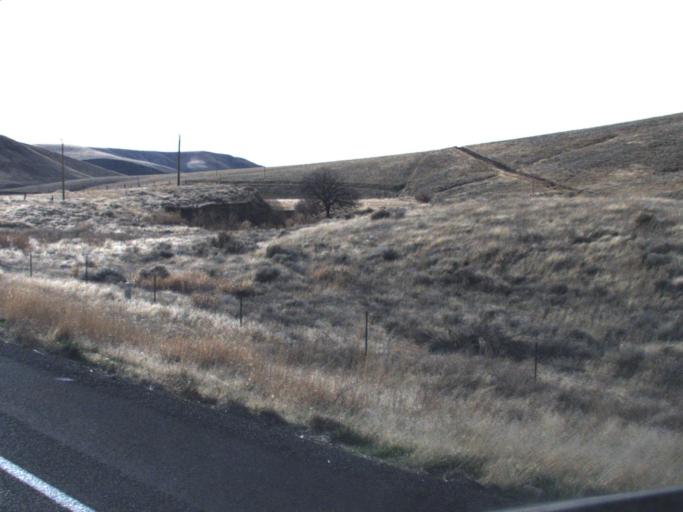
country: US
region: Washington
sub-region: Columbia County
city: Dayton
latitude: 46.5157
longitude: -117.9418
